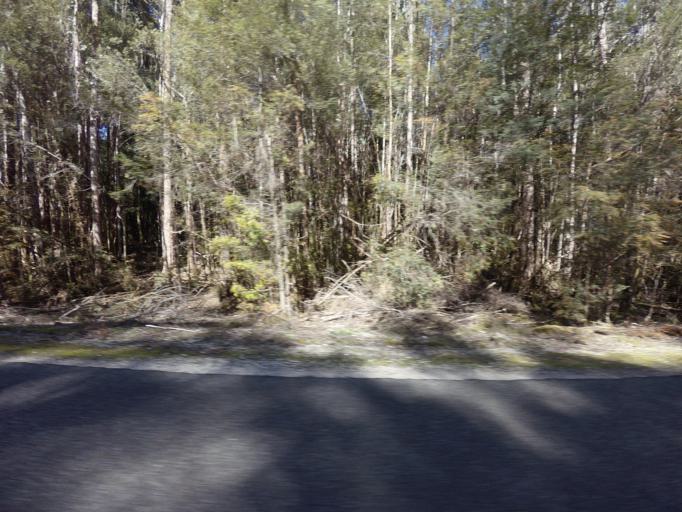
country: AU
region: Tasmania
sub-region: Derwent Valley
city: New Norfolk
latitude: -42.7388
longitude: 146.4212
